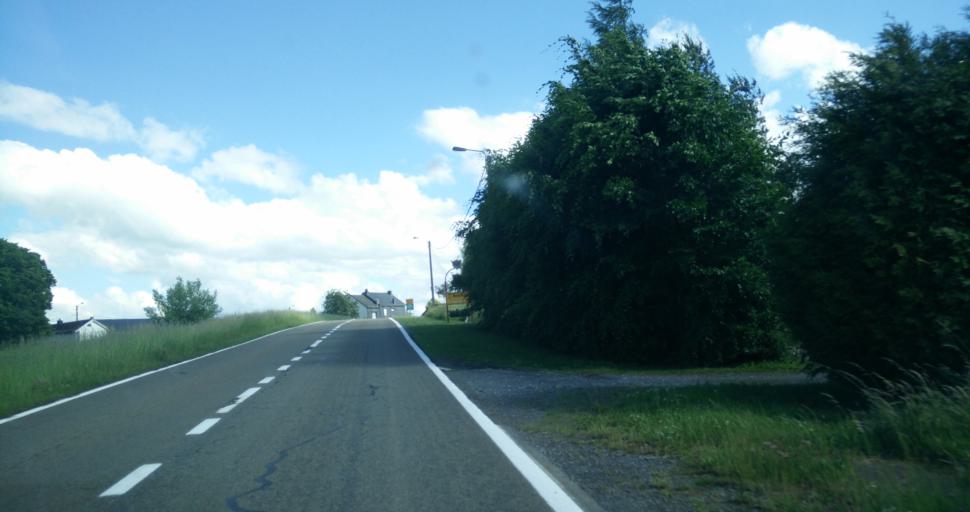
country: BE
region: Wallonia
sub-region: Province du Luxembourg
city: Bertogne
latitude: 50.1673
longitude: 5.6753
